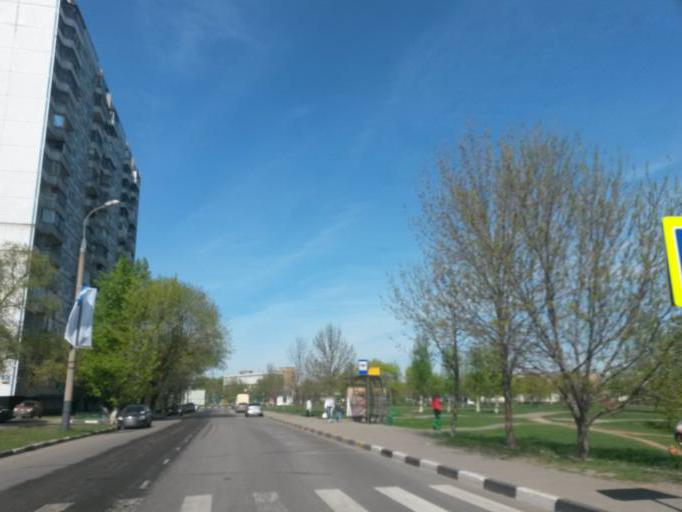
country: RU
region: Moscow
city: Mar'ino
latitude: 55.6501
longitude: 37.7267
